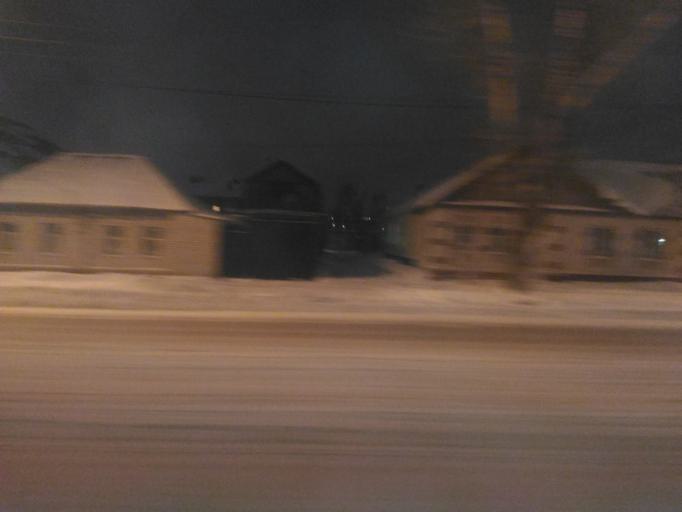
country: RU
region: Ulyanovsk
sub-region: Ulyanovskiy Rayon
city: Ulyanovsk
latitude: 54.3254
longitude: 48.3697
